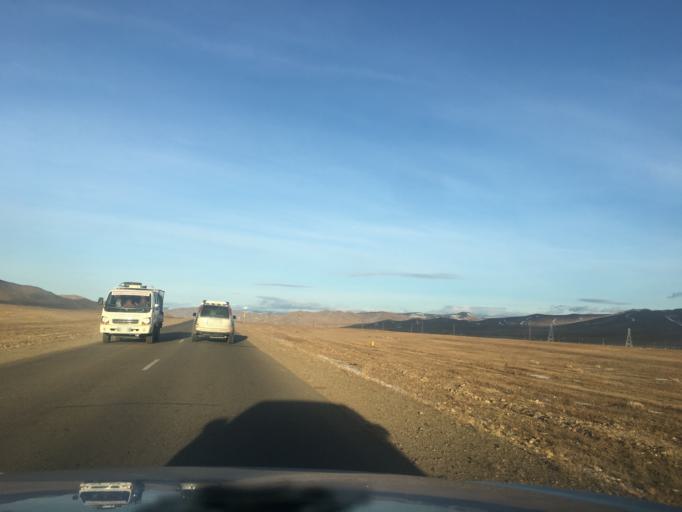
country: MN
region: Central Aimak
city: Mandal
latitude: 48.0886
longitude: 106.5984
